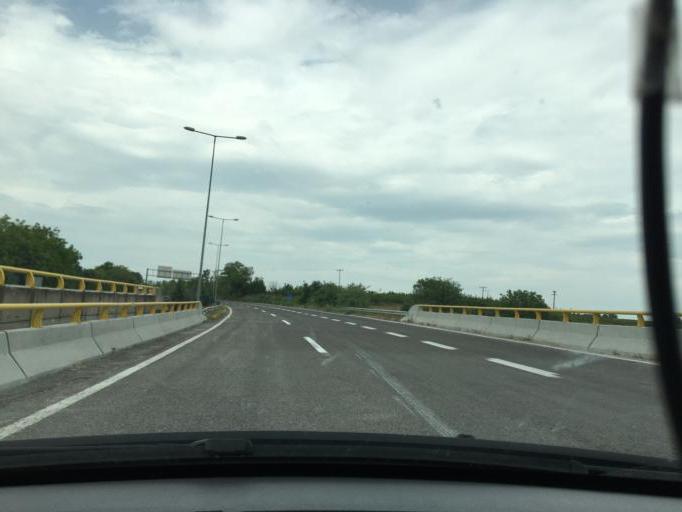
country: MK
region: Gradsko
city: Gradsko
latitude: 41.5624
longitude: 21.9557
